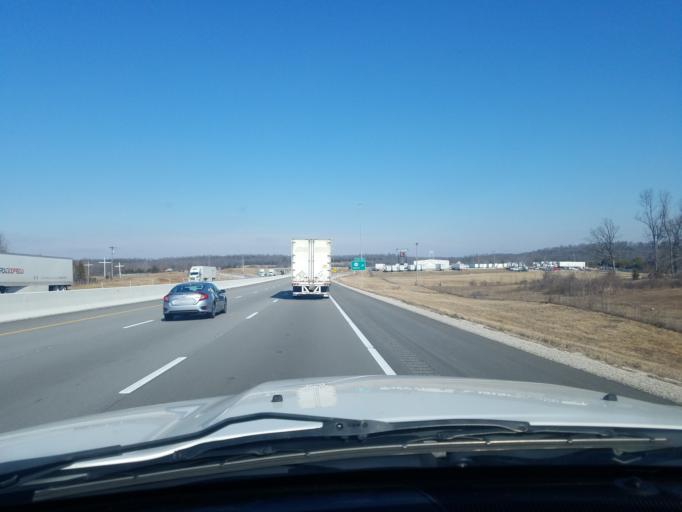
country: US
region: Kentucky
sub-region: Hart County
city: Munfordville
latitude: 37.4526
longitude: -85.8830
